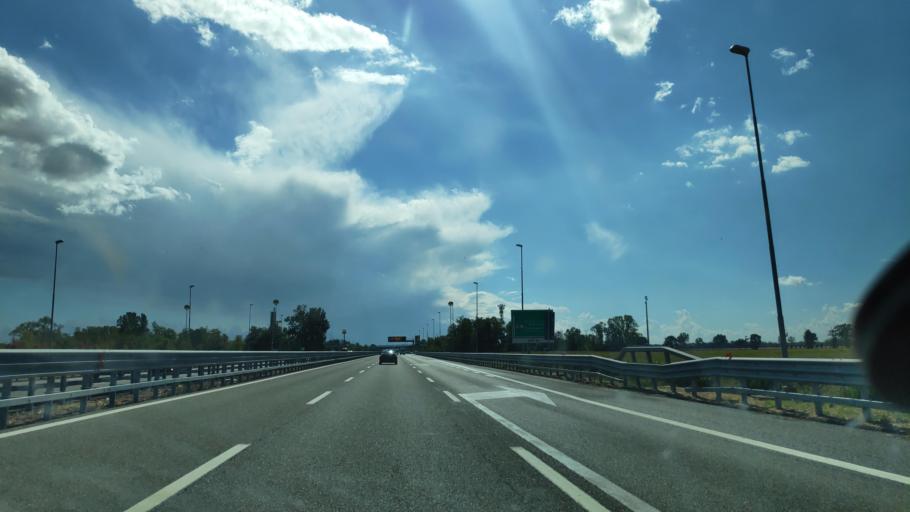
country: IT
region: Piedmont
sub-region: Provincia di Alessandria
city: Tortona
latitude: 44.9379
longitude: 8.8551
